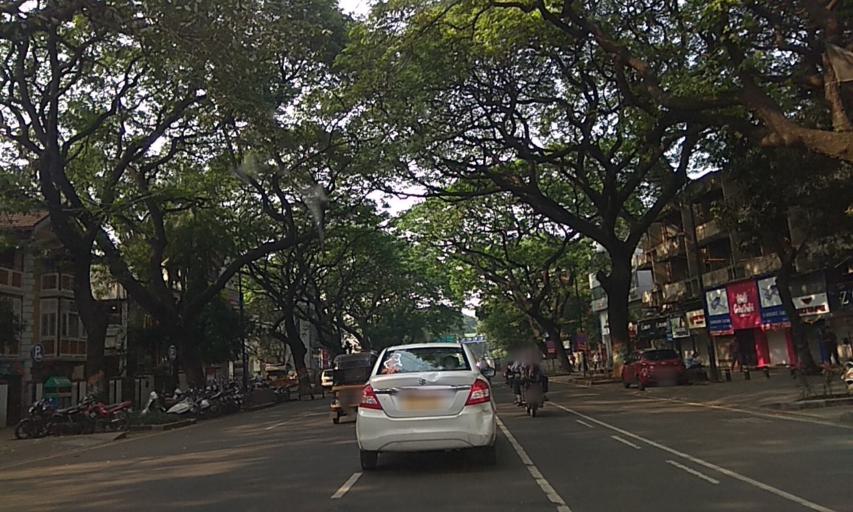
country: IN
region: Maharashtra
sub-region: Pune Division
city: Pune
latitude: 18.5188
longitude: 73.8448
